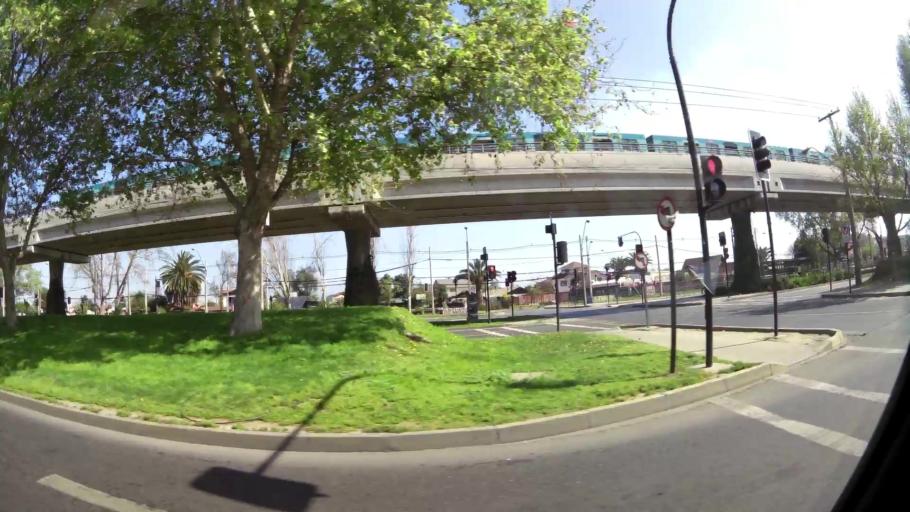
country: CL
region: Santiago Metropolitan
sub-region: Provincia de Santiago
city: Lo Prado
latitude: -33.4775
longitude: -70.7414
